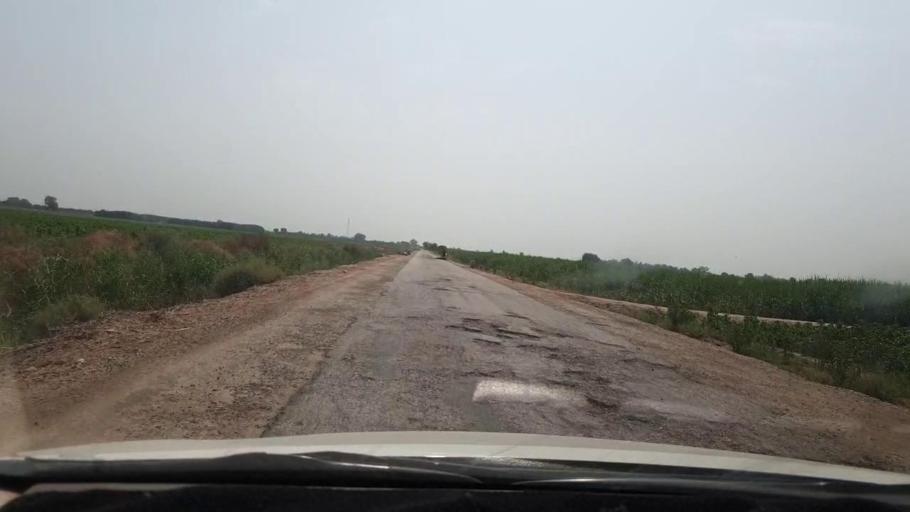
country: PK
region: Sindh
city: Rohri
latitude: 27.5387
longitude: 69.0144
